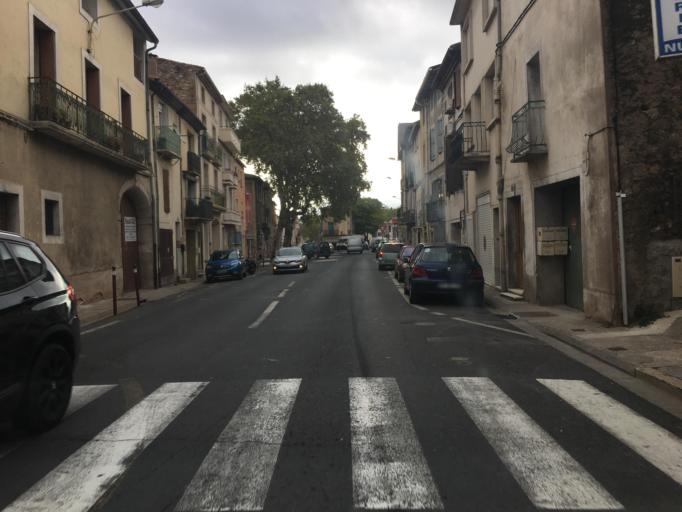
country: FR
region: Languedoc-Roussillon
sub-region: Departement de l'Herault
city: Nebian
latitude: 43.6255
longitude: 3.4326
